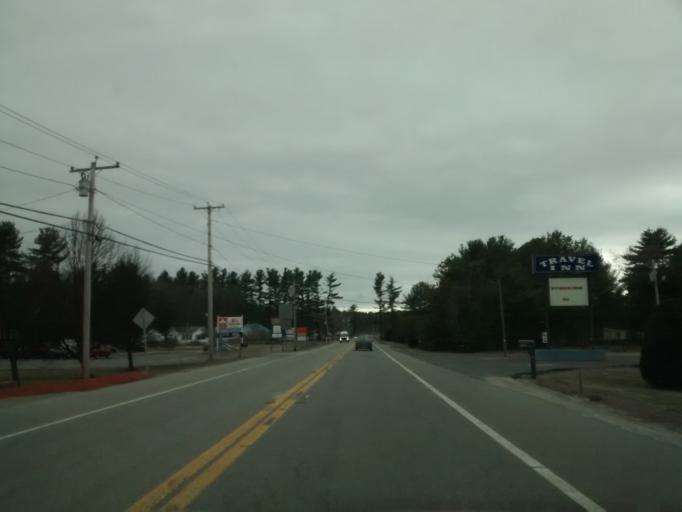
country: US
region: Massachusetts
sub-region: Franklin County
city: Orange
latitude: 42.5577
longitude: -72.2870
